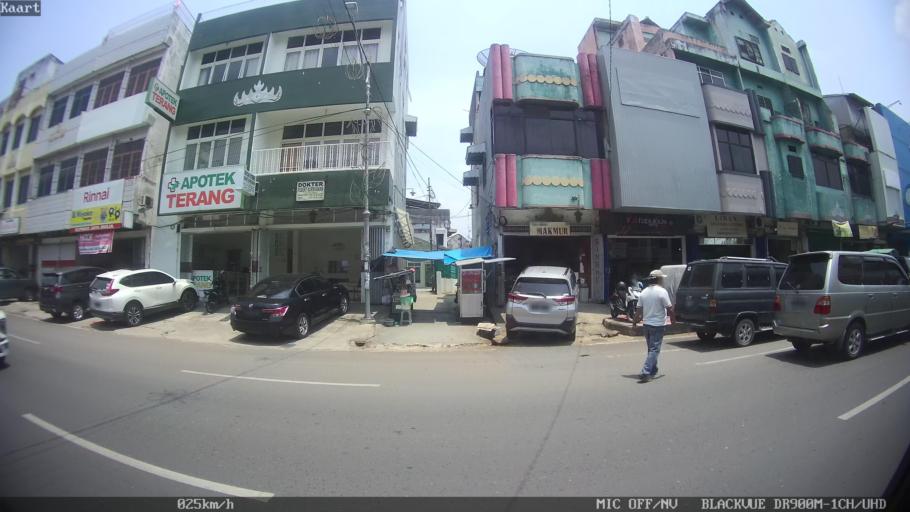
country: ID
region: Lampung
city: Bandarlampung
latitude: -5.4134
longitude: 105.2555
